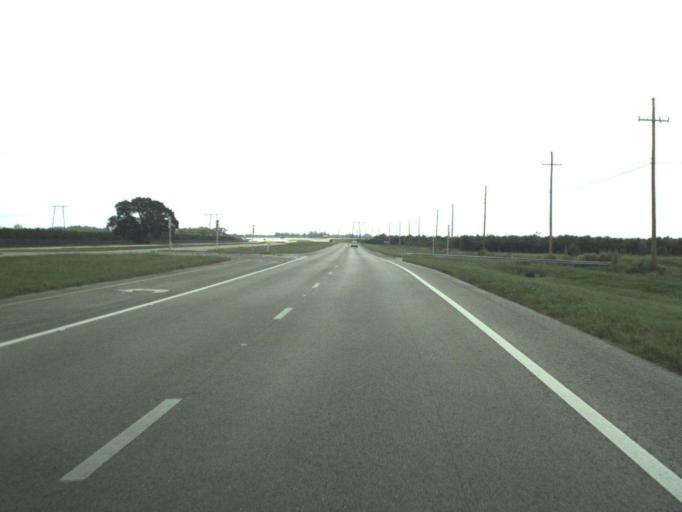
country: US
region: Florida
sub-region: Saint Lucie County
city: Fort Pierce South
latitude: 27.3768
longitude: -80.4821
